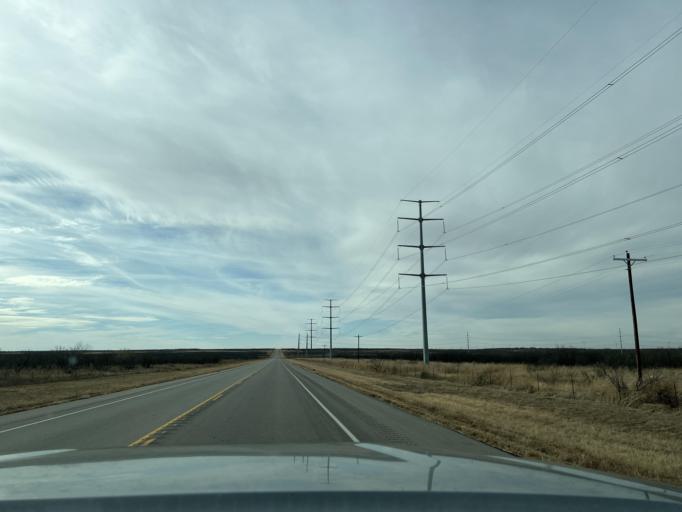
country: US
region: Texas
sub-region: Jones County
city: Stamford
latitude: 32.7504
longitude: -99.6441
